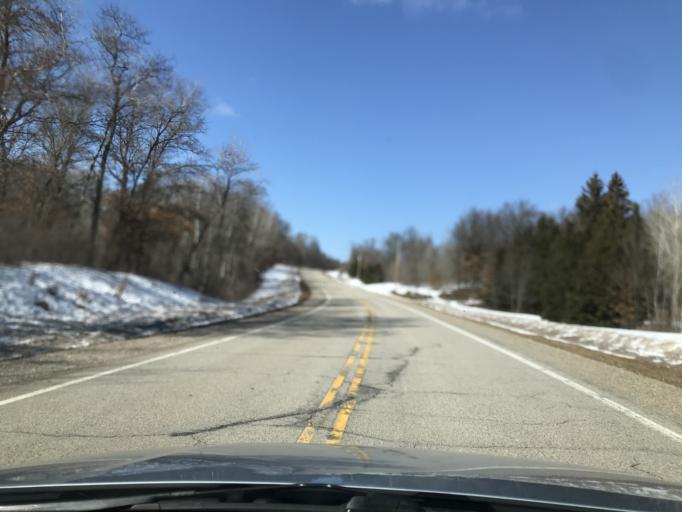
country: US
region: Wisconsin
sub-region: Marinette County
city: Niagara
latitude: 45.3372
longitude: -88.1006
